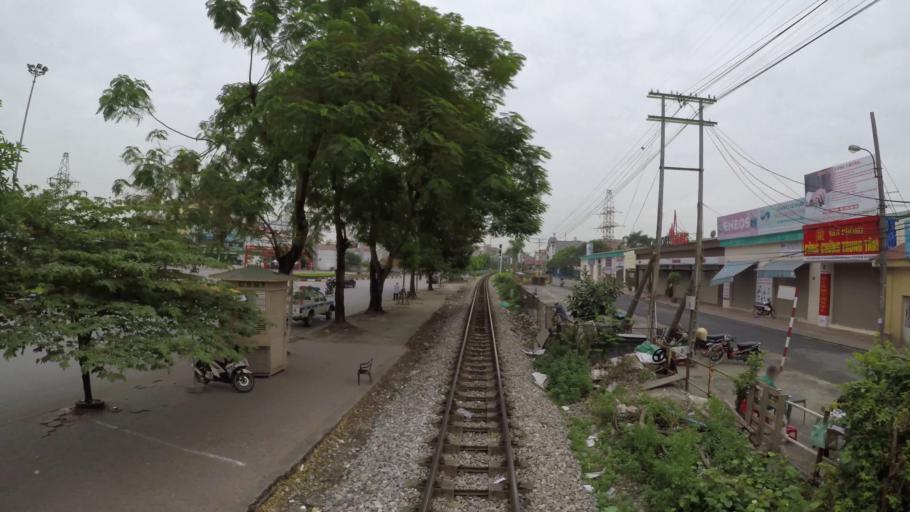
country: VN
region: Hai Phong
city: An Duong
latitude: 20.8755
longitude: 106.6370
